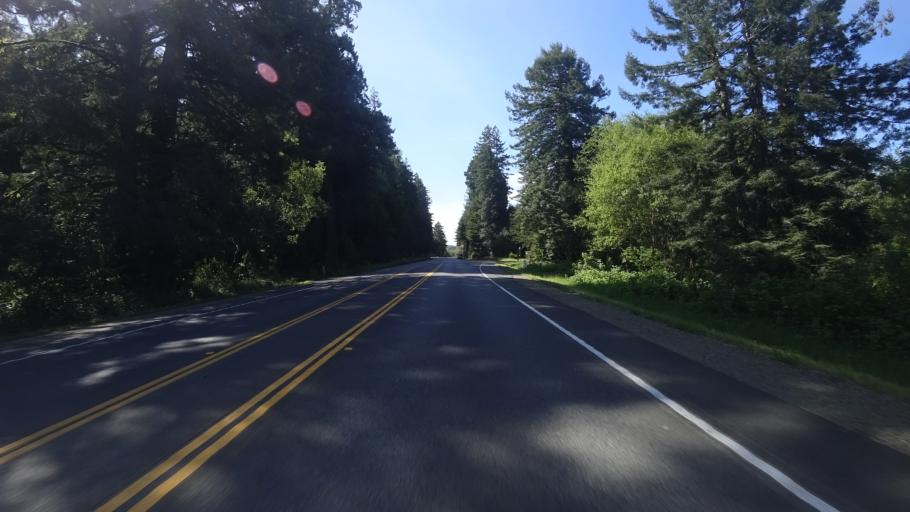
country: US
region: California
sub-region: Del Norte County
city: Bertsch-Oceanview
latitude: 41.8847
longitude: -124.1368
